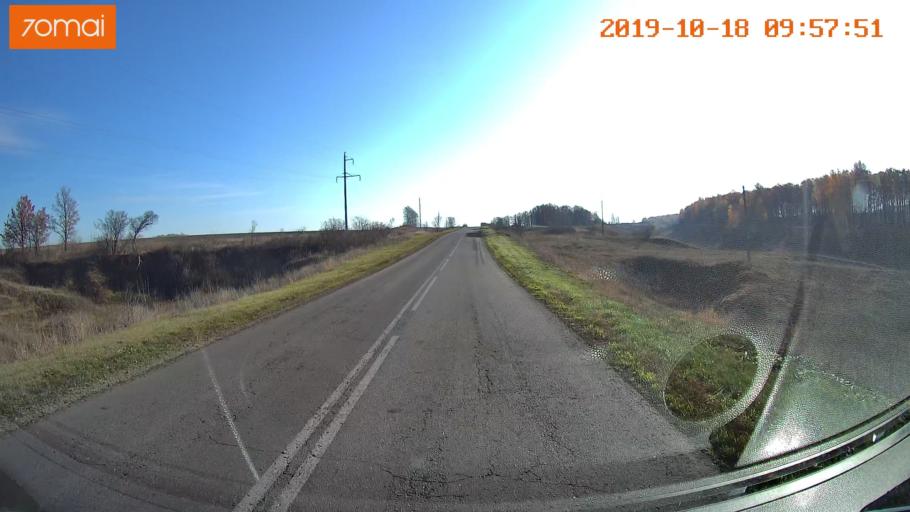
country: RU
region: Tula
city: Kurkino
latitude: 53.3770
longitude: 38.4275
